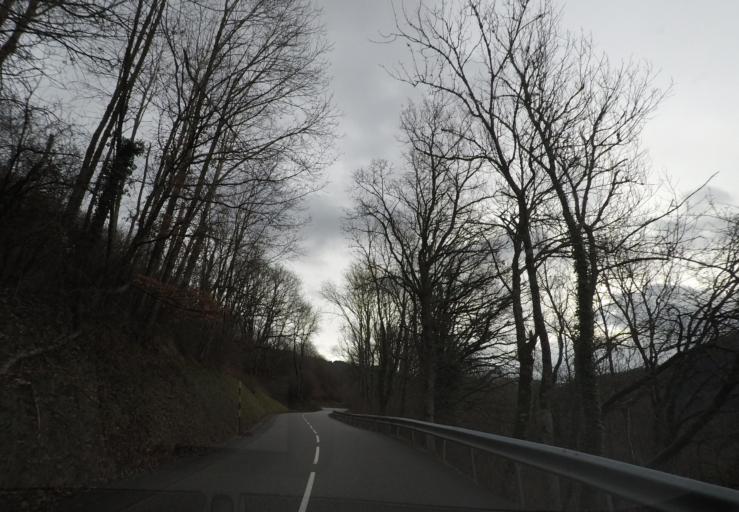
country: FR
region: Rhone-Alpes
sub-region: Departement de la Haute-Savoie
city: Chatillon-sur-Cluses
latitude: 46.0769
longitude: 6.5972
